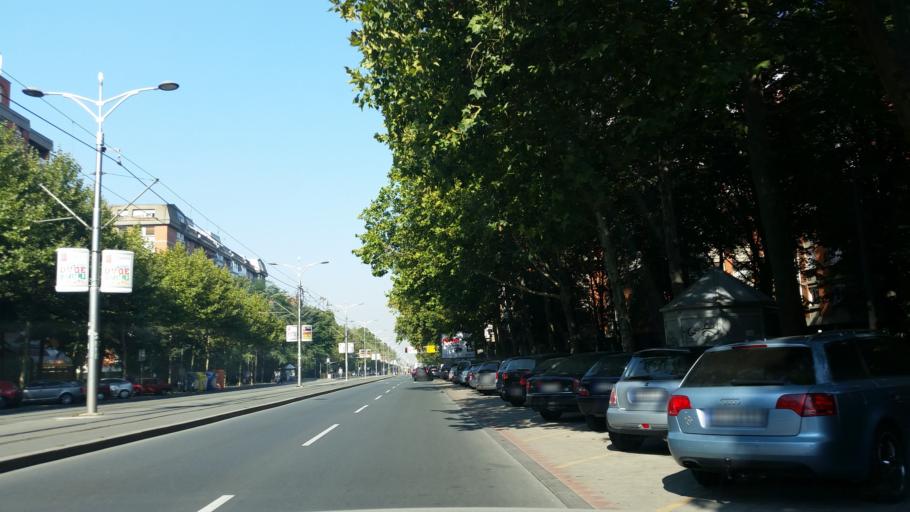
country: RS
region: Central Serbia
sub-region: Belgrade
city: Palilula
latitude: 44.7947
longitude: 20.5012
